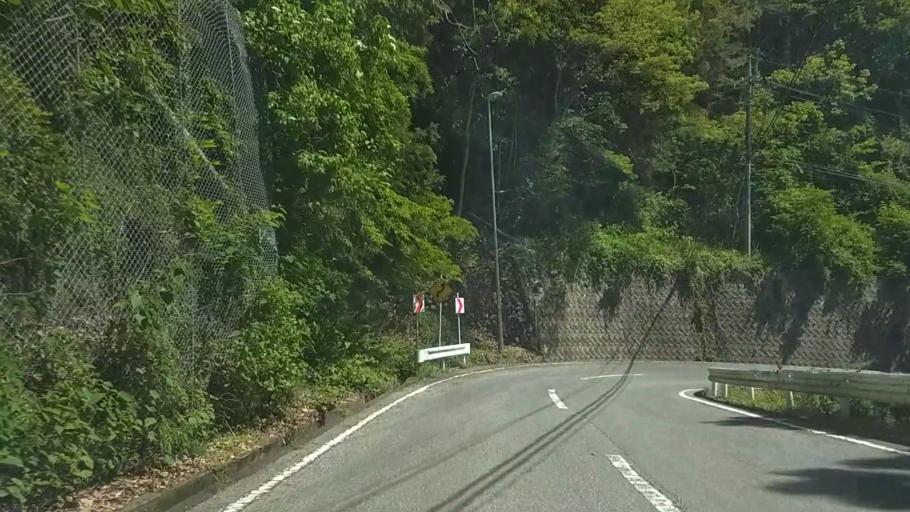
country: JP
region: Yamanashi
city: Ryuo
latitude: 35.5091
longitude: 138.4039
